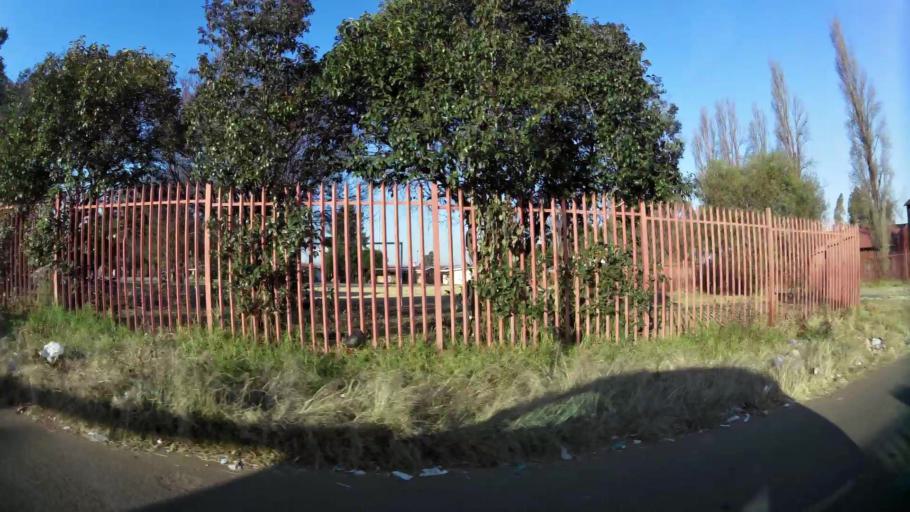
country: ZA
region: Gauteng
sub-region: City of Johannesburg Metropolitan Municipality
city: Soweto
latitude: -26.2530
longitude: 27.8786
